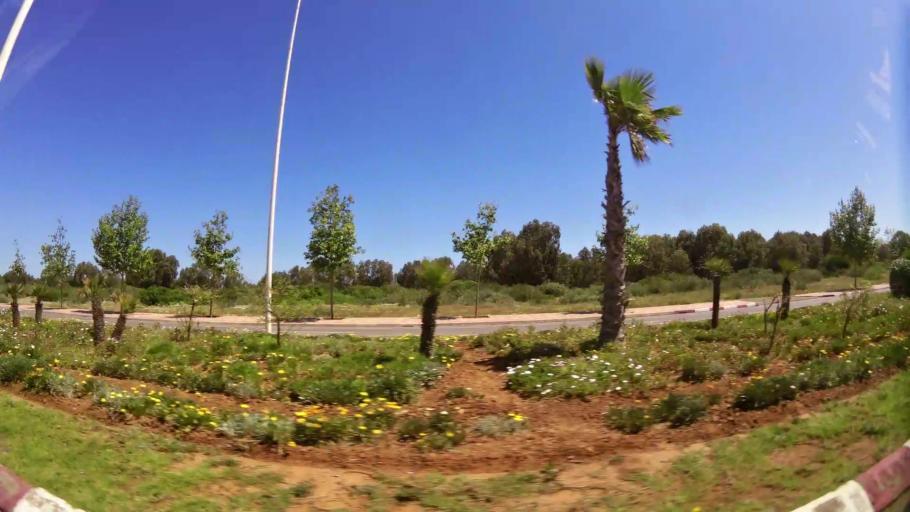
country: MA
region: Oriental
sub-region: Berkane-Taourirt
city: Madagh
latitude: 35.1012
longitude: -2.2905
